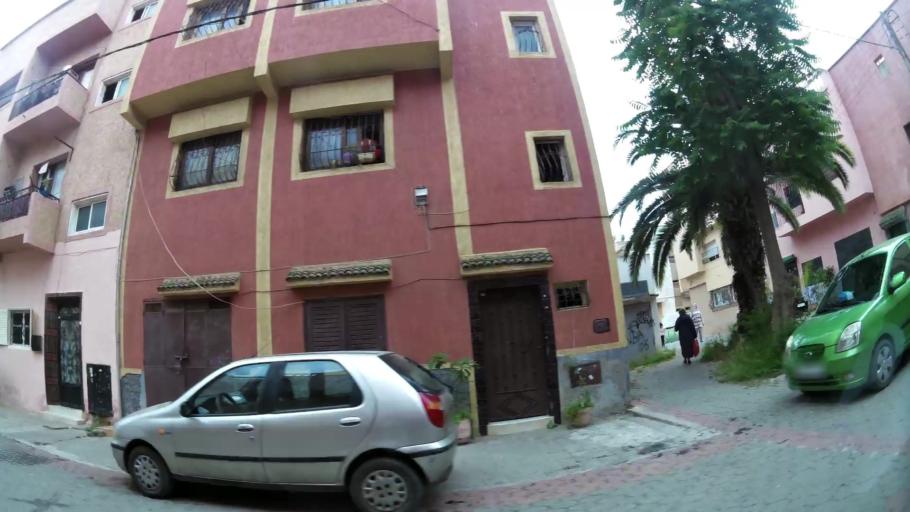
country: MA
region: Rabat-Sale-Zemmour-Zaer
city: Sale
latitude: 34.0437
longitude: -6.7958
